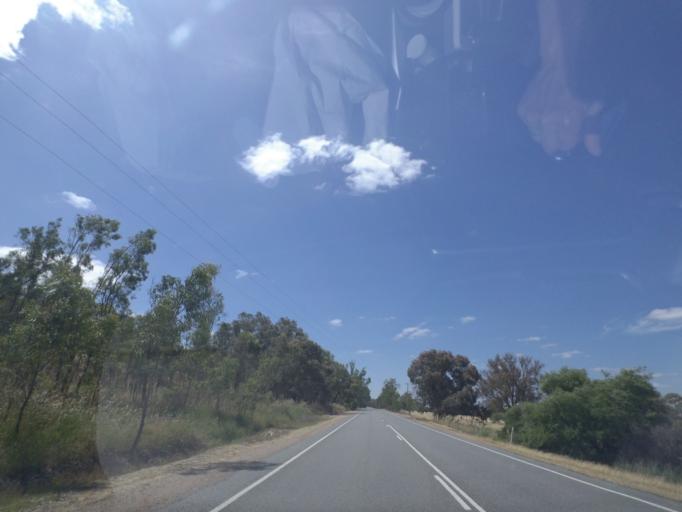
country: AU
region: Victoria
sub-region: Wangaratta
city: Wangaratta
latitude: -36.4558
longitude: 146.2368
